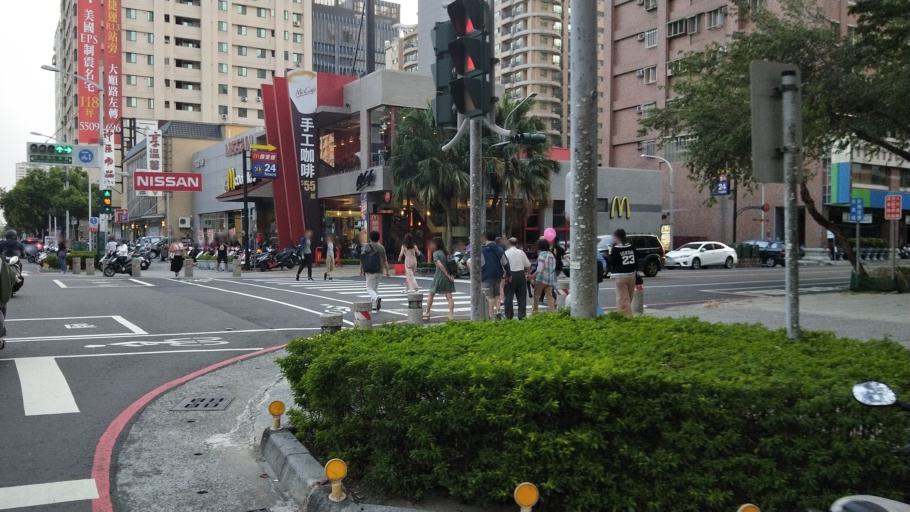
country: TW
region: Kaohsiung
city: Kaohsiung
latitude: 22.6647
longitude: 120.3033
